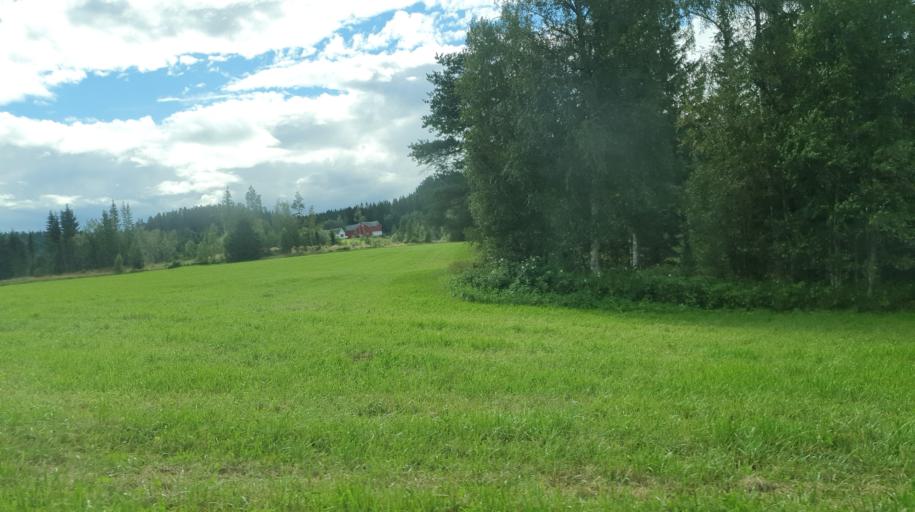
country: NO
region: Nord-Trondelag
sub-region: Levanger
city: Skogn
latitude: 63.6029
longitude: 11.2745
